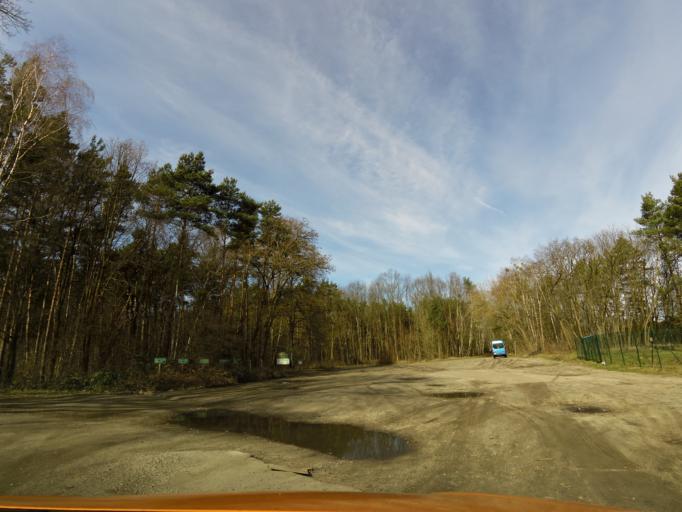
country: DE
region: Brandenburg
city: Michendorf
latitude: 52.3551
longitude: 13.0441
